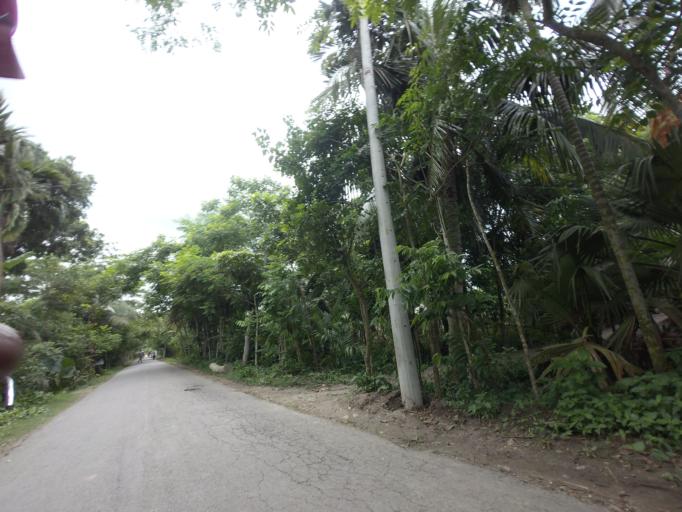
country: BD
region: Khulna
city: Kalia
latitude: 23.0404
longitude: 89.6436
